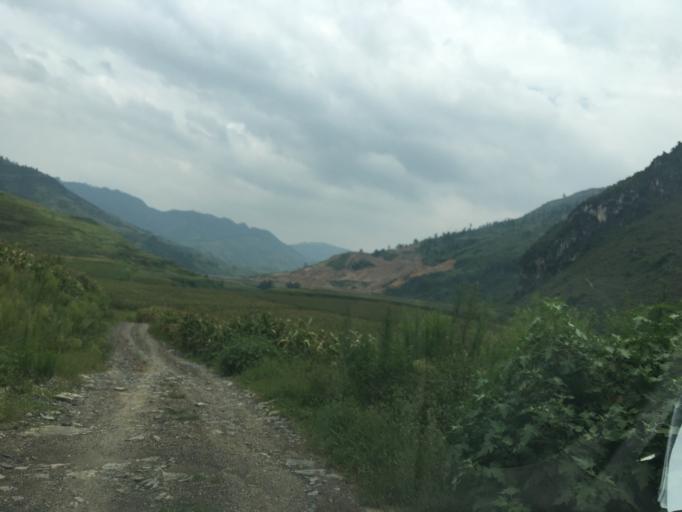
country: CN
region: Guangxi Zhuangzu Zizhiqu
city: Xinzhou
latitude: 25.1788
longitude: 105.7323
